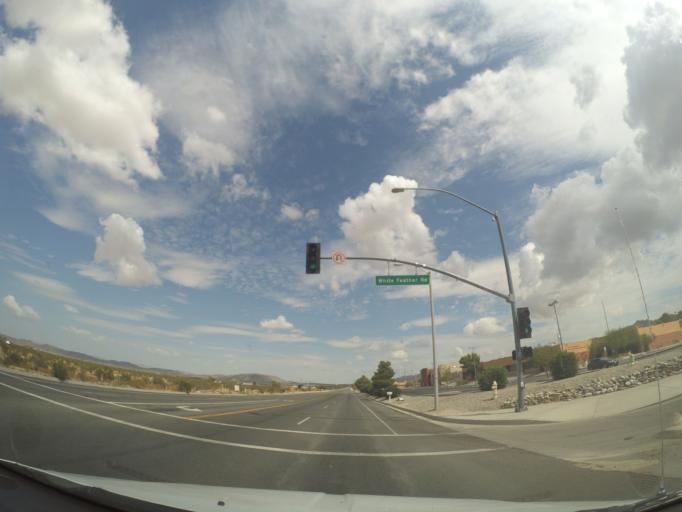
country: US
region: California
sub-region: San Bernardino County
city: Joshua Tree
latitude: 34.1351
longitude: -116.2773
